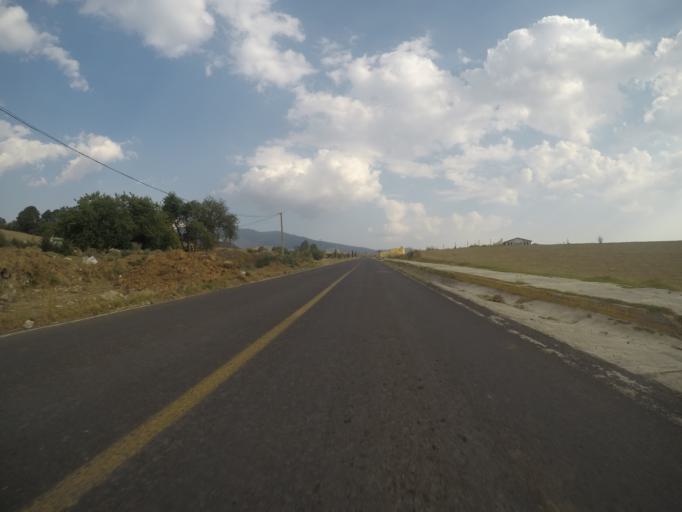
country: MX
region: Mexico
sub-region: Xalatlaco
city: El Aguila (La Mesa)
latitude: 19.1615
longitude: -99.4054
